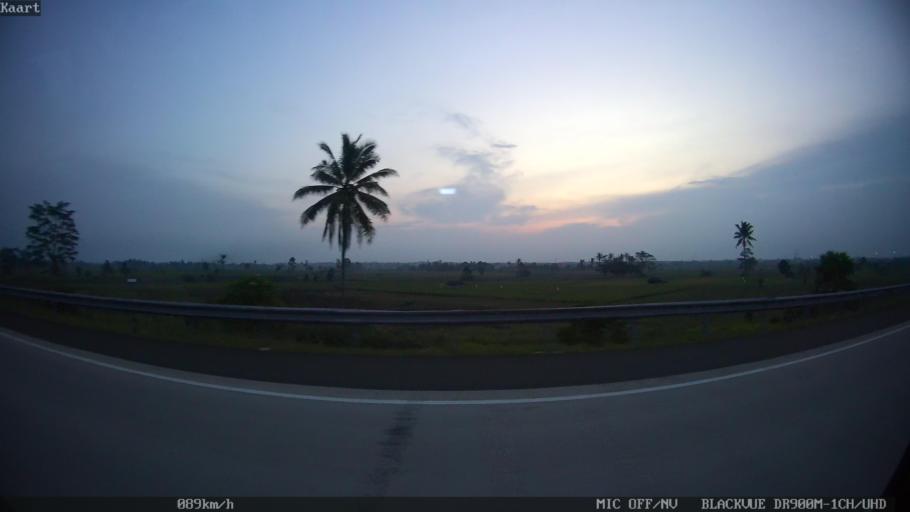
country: ID
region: Lampung
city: Sidorejo
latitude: -5.6136
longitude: 105.5593
